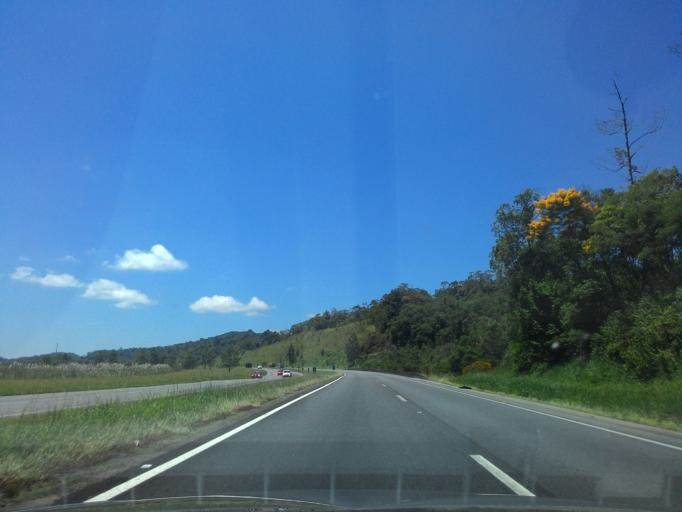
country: BR
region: Parana
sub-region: Antonina
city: Antonina
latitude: -25.0977
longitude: -48.6567
